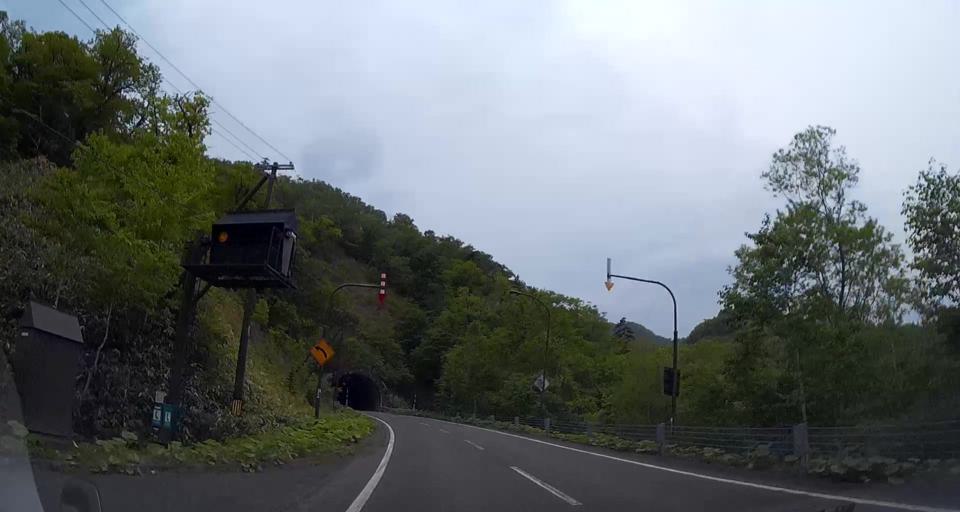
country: JP
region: Hokkaido
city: Shiraoi
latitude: 42.6575
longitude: 141.1806
